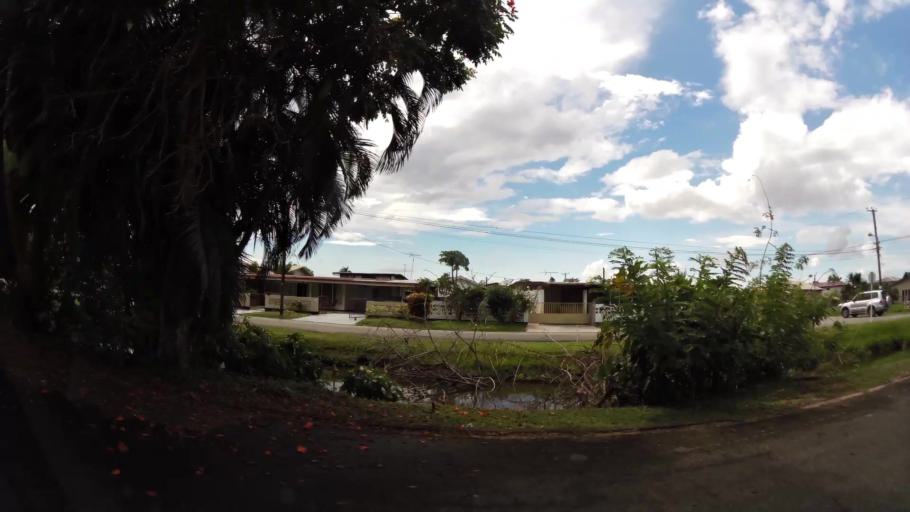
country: SR
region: Paramaribo
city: Paramaribo
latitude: 5.8401
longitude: -55.1294
